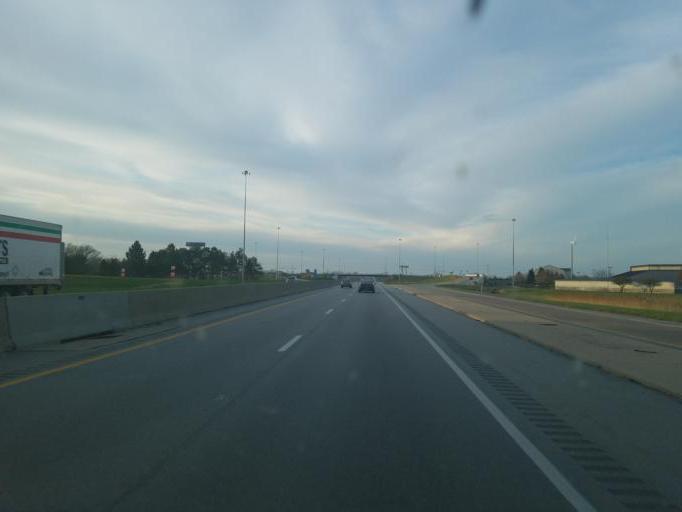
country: US
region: Ohio
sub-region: Wood County
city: Northwood
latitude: 41.6113
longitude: -83.4769
